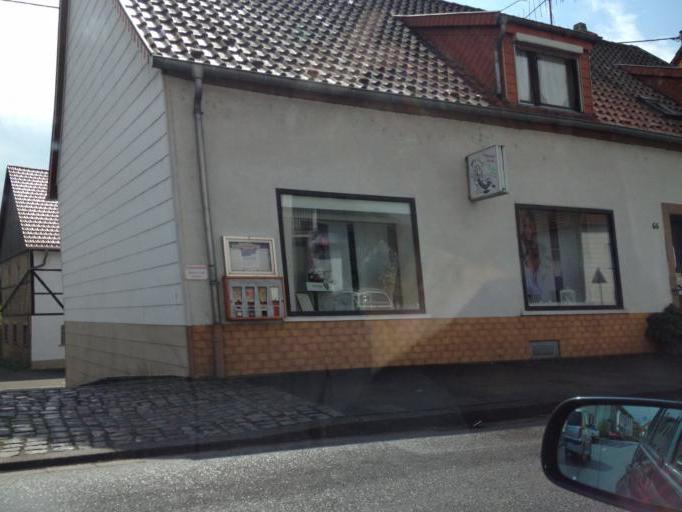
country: DE
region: Saarland
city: Blieskastel
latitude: 49.2626
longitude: 7.2835
